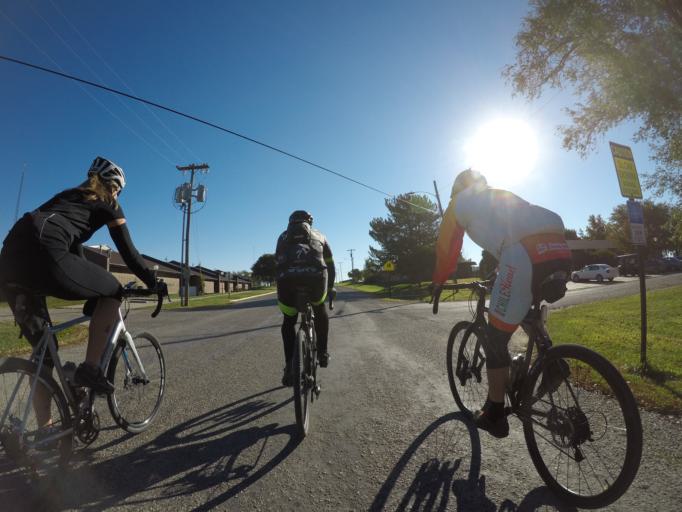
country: US
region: Kansas
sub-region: Morris County
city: Council Grove
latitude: 38.8641
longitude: -96.4859
